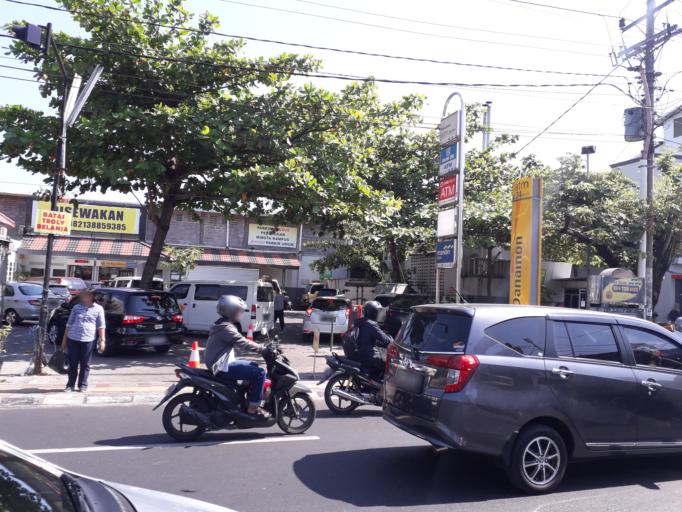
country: ID
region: Daerah Istimewa Yogyakarta
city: Yogyakarta
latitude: -7.7762
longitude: 110.3751
